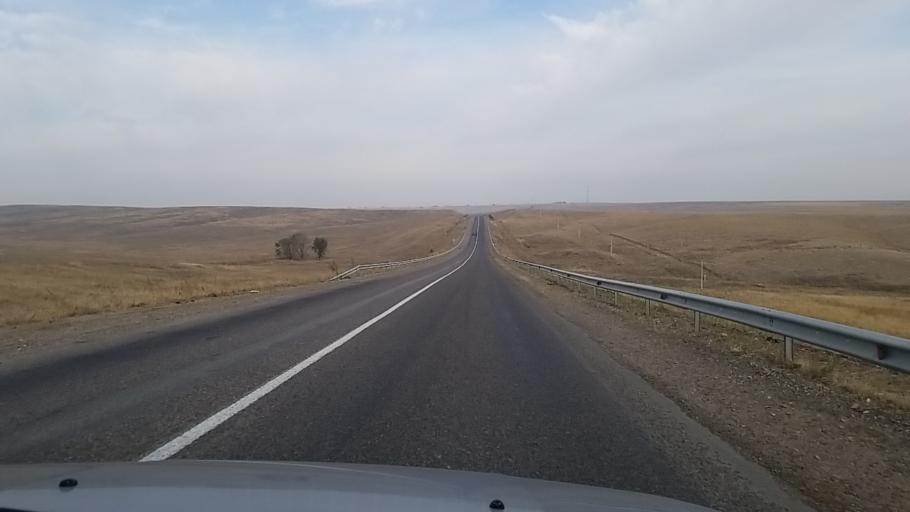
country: KZ
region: Almaty Oblysy
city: Burunday
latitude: 43.4900
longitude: 76.6676
